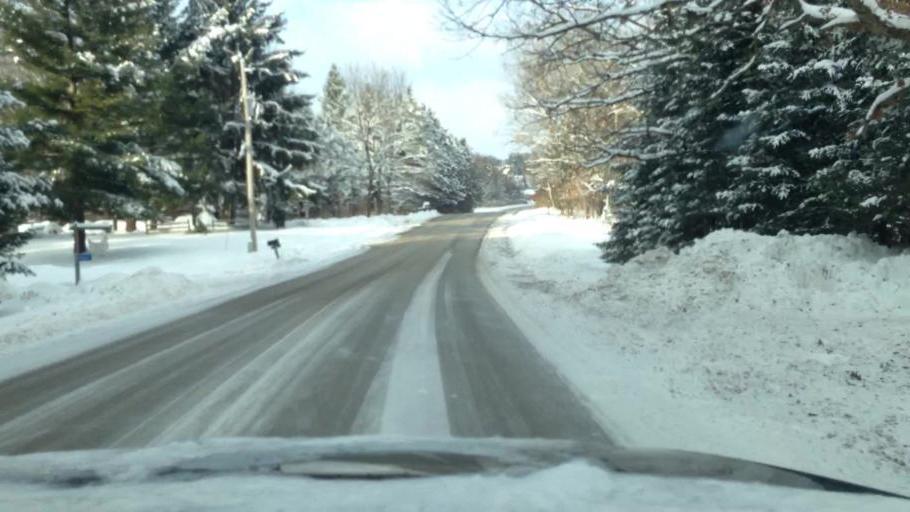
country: US
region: Wisconsin
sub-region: Walworth County
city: East Troy
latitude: 42.8121
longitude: -88.4270
